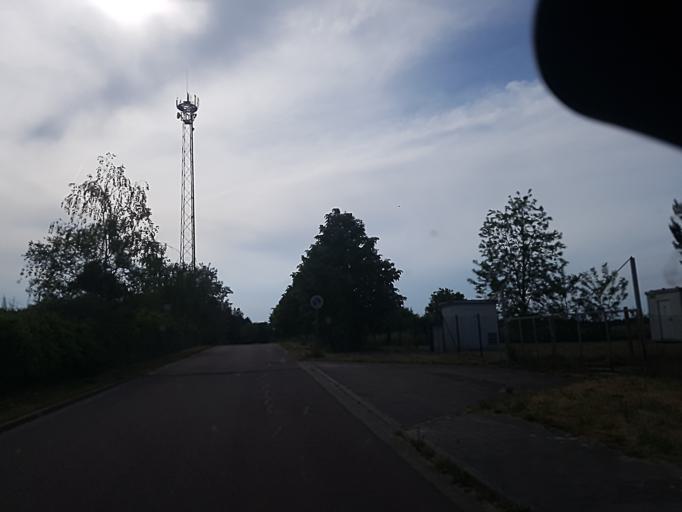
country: DE
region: Saxony-Anhalt
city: Zahna
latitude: 51.9197
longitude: 12.7759
